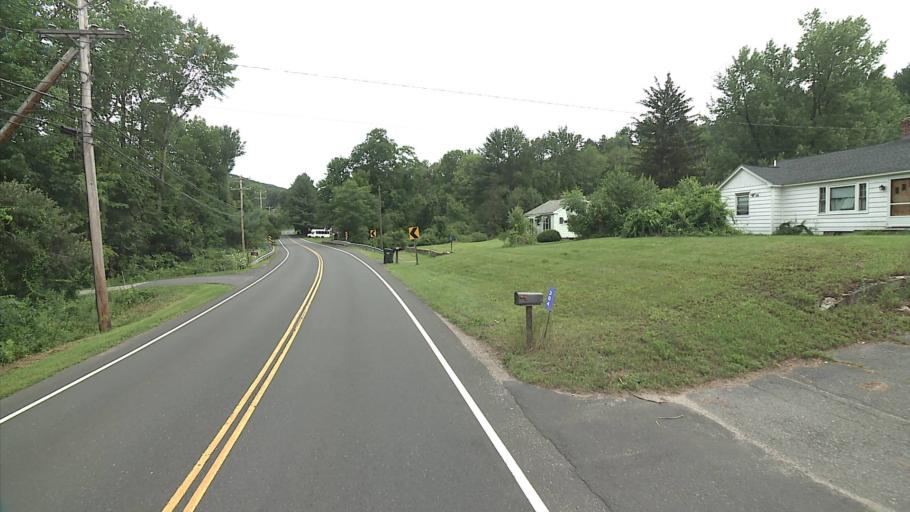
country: US
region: Connecticut
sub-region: Litchfield County
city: Winsted
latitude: 41.9806
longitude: -73.0445
